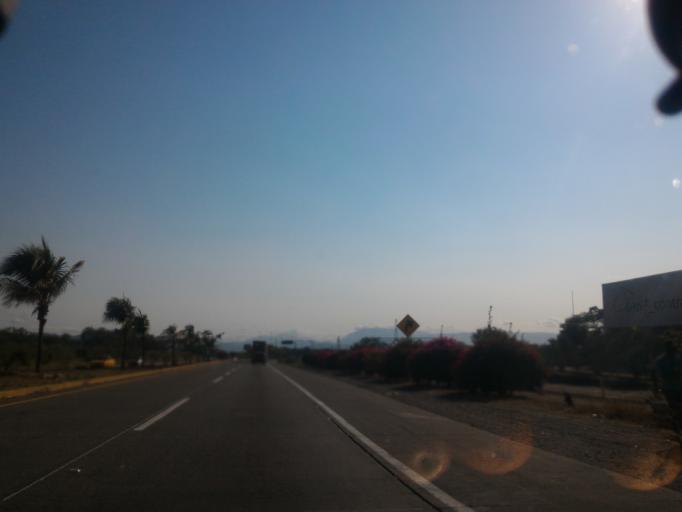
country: MX
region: Colima
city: Colima
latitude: 19.2601
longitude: -103.6834
